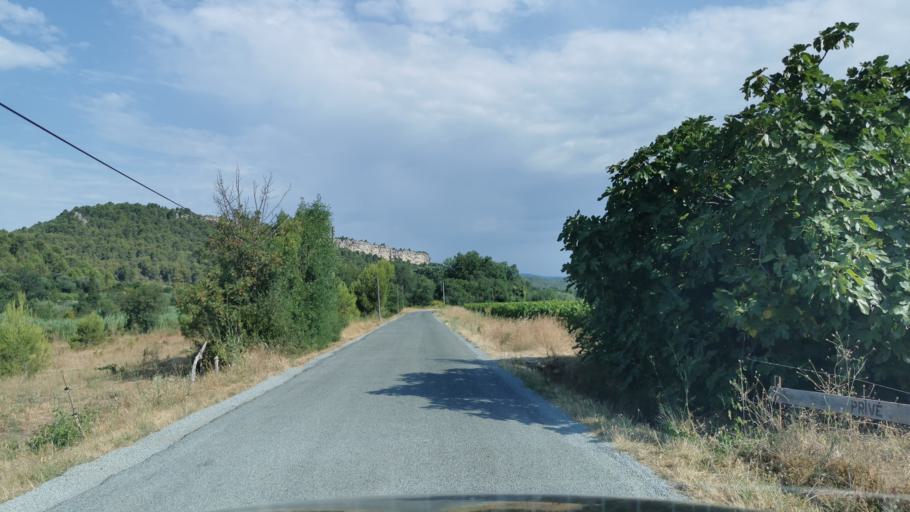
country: FR
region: Languedoc-Roussillon
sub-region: Departement de l'Aude
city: Bize-Minervois
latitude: 43.3252
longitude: 2.8796
